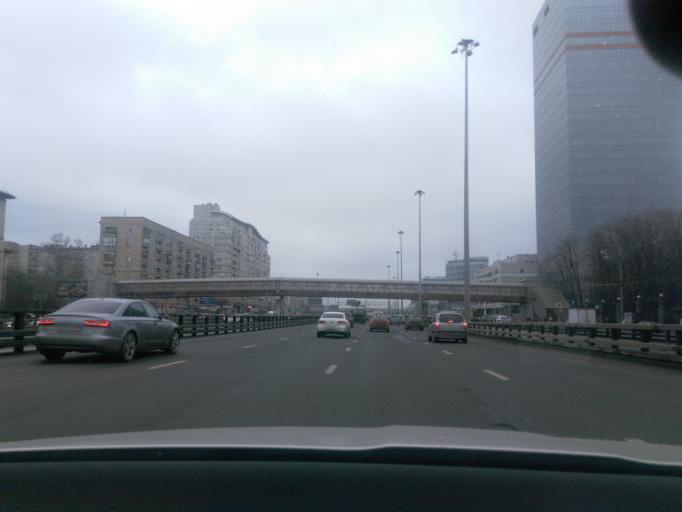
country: RU
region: Moscow
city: Sokol
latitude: 55.7985
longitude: 37.5361
